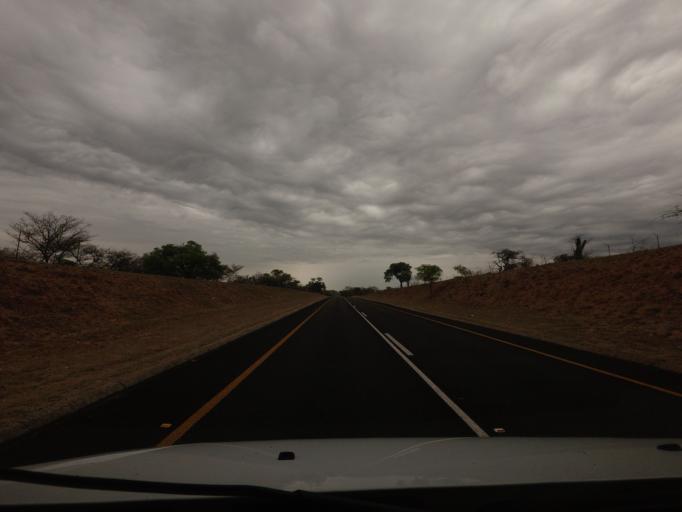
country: ZA
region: Limpopo
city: Thulamahashi
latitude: -24.5674
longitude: 31.0905
